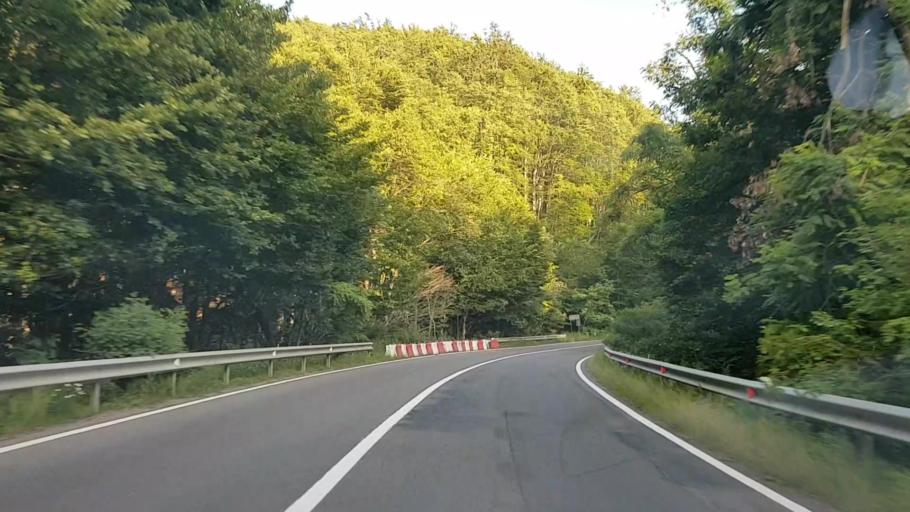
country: RO
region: Harghita
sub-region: Comuna Corund
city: Corund
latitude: 46.4470
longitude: 25.2278
